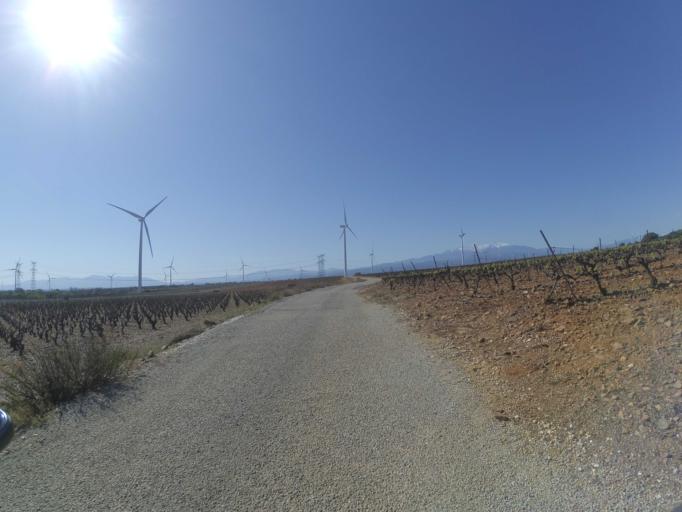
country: FR
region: Languedoc-Roussillon
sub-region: Departement des Pyrenees-Orientales
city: Pezilla-la-Riviere
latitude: 42.7297
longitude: 2.7737
